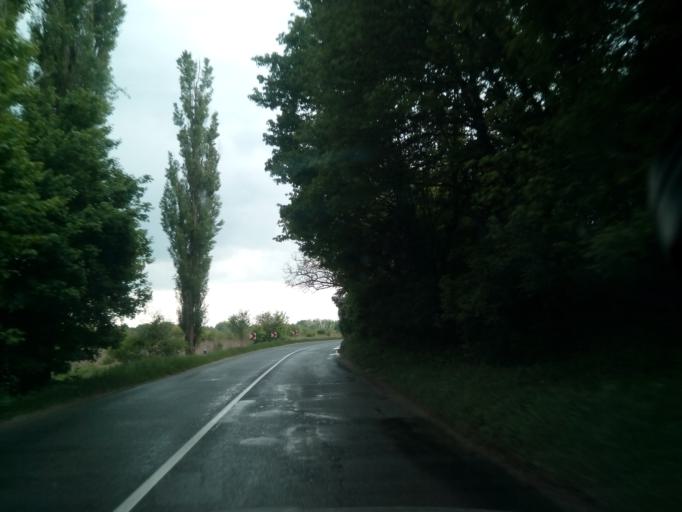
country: SK
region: Kosicky
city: Kosice
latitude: 48.7584
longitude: 21.2484
